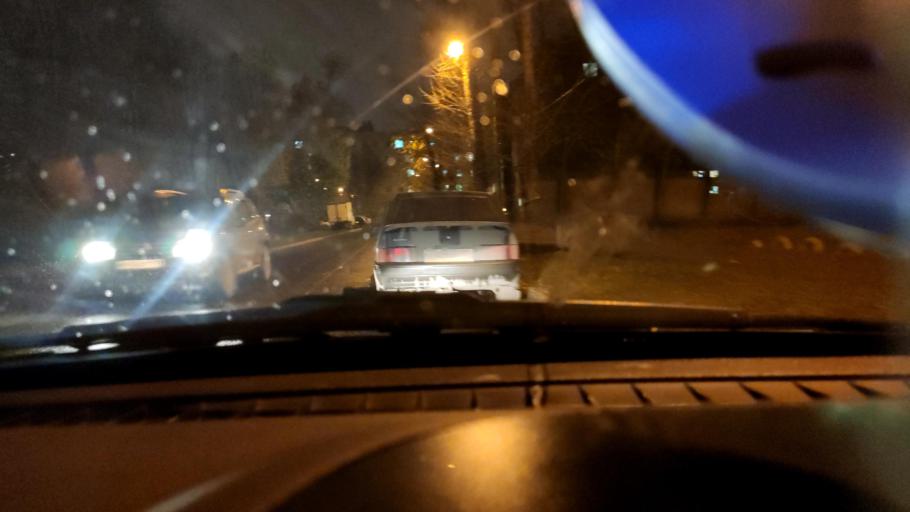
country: RU
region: Perm
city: Perm
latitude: 57.9835
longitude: 56.1874
